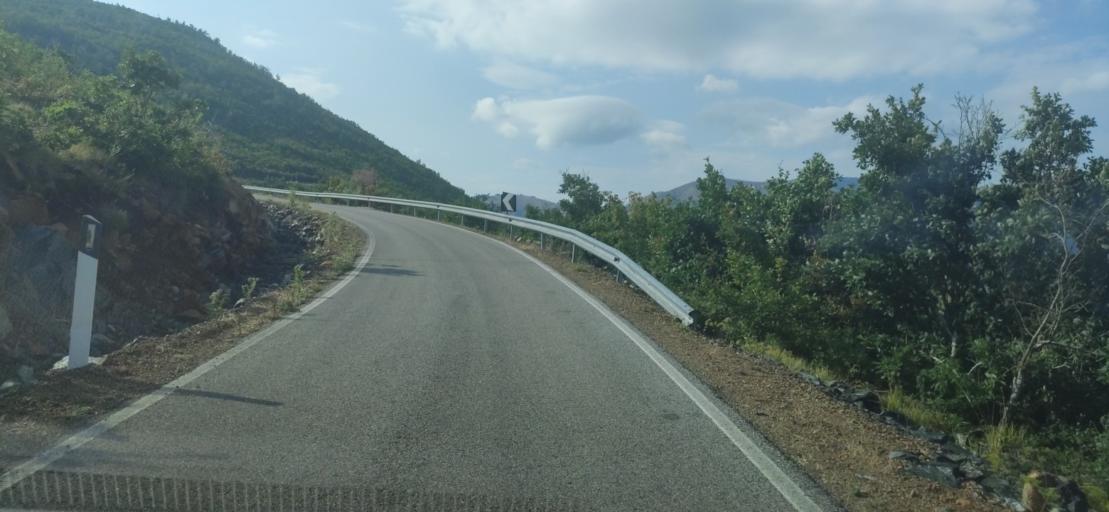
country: AL
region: Shkoder
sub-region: Rrethi i Pukes
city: Iballe
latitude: 42.1722
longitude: 20.0006
